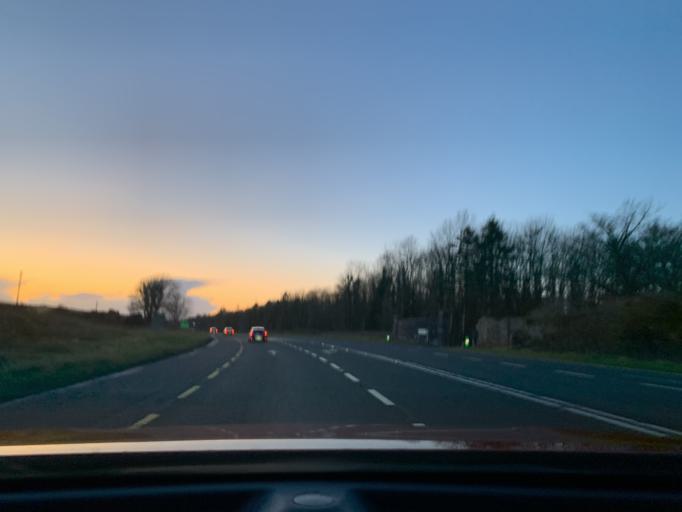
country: IE
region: Connaught
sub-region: Roscommon
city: Boyle
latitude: 53.9704
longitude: -8.2062
